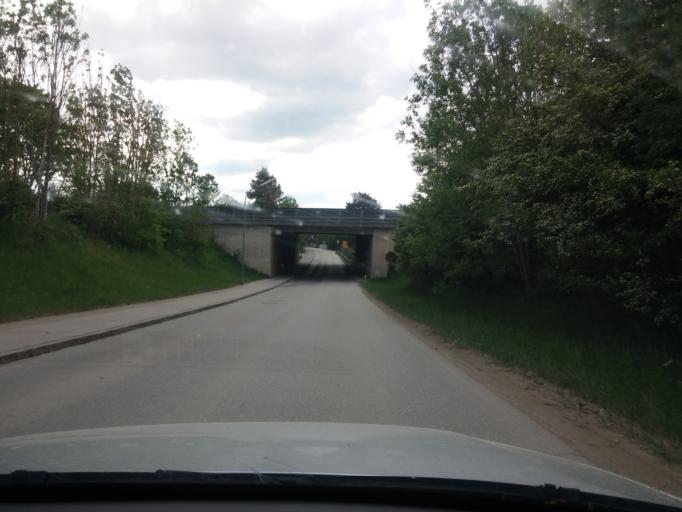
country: DE
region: Bavaria
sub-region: Upper Bavaria
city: Holzkirchen
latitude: 47.8992
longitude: 11.7229
